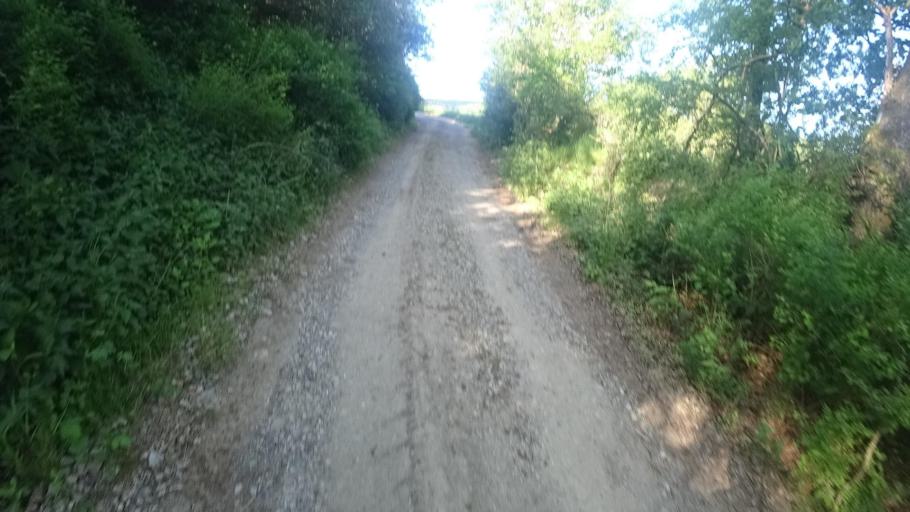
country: DE
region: Rheinland-Pfalz
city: Berg
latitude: 50.5415
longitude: 6.9669
